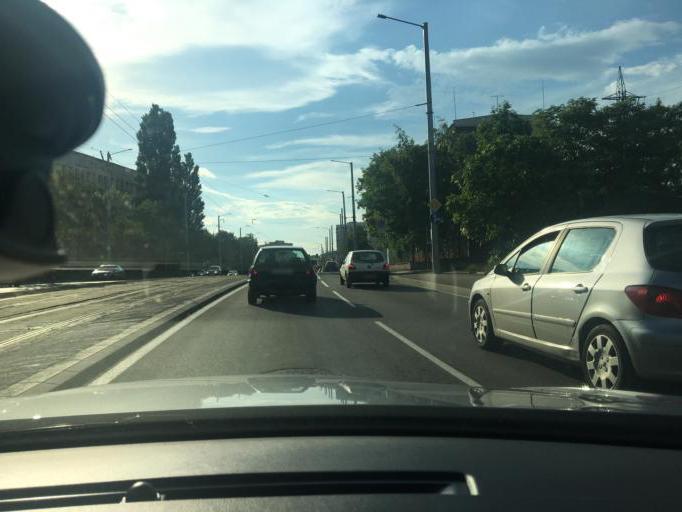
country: BG
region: Sofia-Capital
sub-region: Stolichna Obshtina
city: Sofia
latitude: 42.6760
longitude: 23.3719
